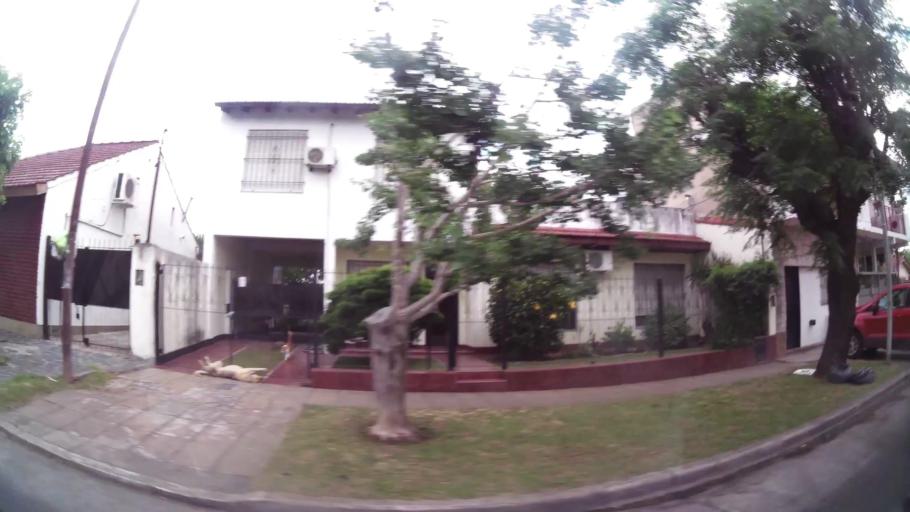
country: AR
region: Buenos Aires
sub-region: Partido de Tigre
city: Tigre
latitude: -34.4636
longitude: -58.6459
